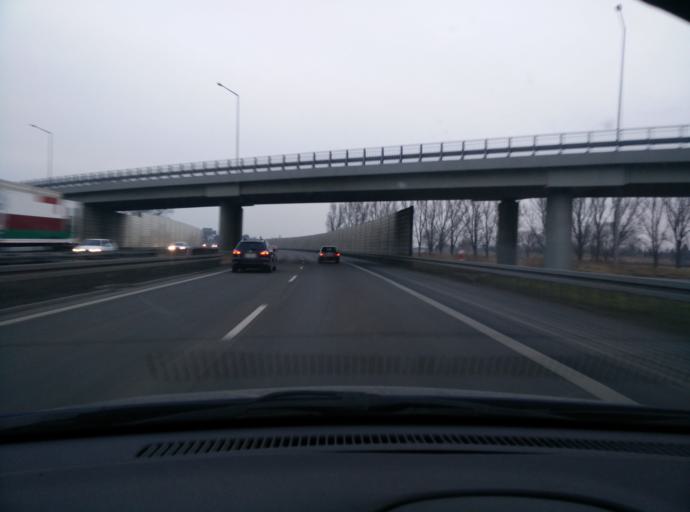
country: PL
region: Greater Poland Voivodeship
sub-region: Powiat poznanski
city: Daszewice
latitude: 52.3403
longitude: 17.0015
